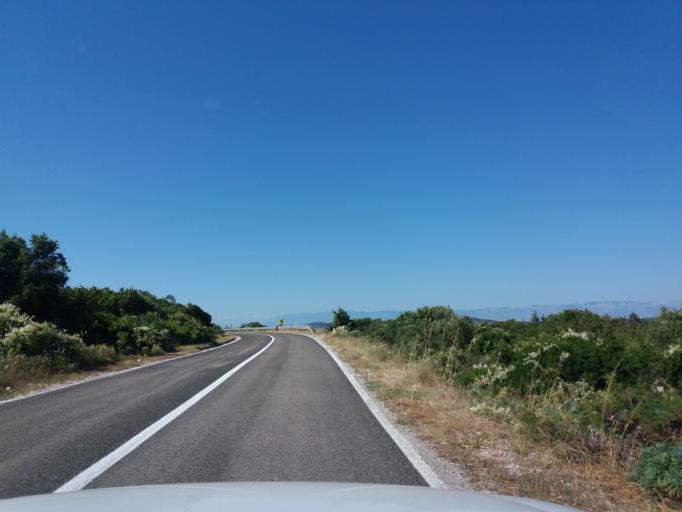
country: HR
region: Zadarska
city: Ugljan
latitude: 44.1023
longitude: 14.9406
